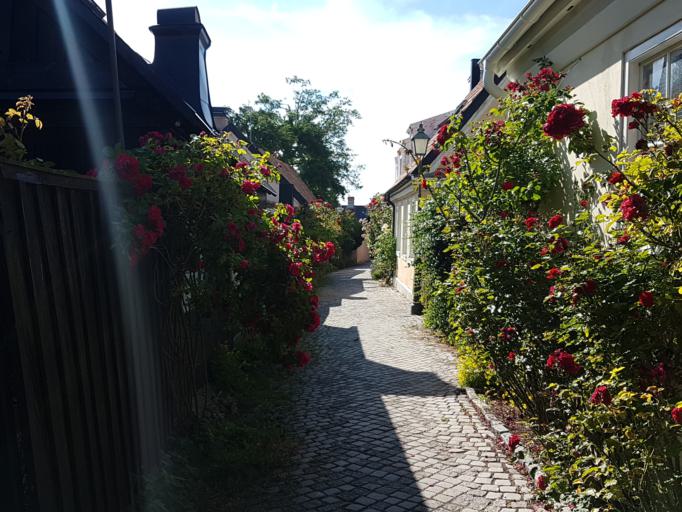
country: SE
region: Gotland
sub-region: Gotland
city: Visby
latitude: 57.6428
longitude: 18.2934
